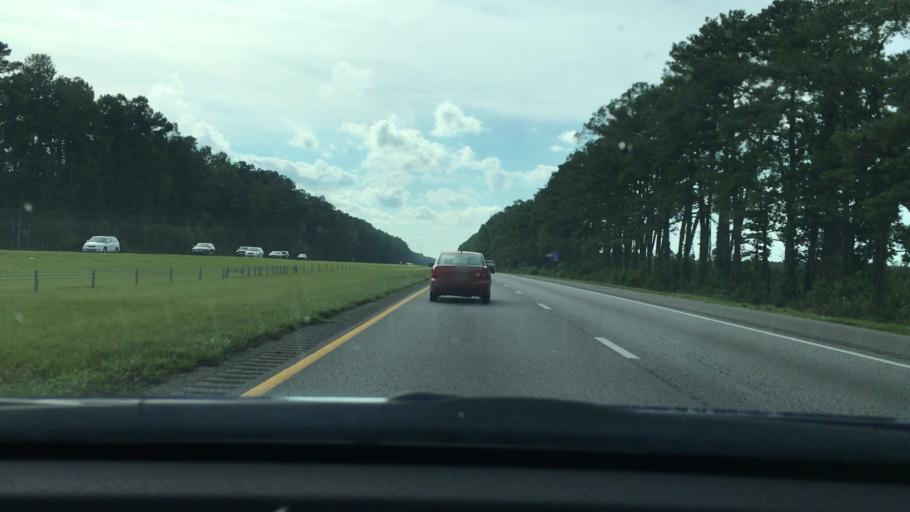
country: US
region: South Carolina
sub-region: Dorchester County
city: Summerville
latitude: 33.0848
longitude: -80.2120
